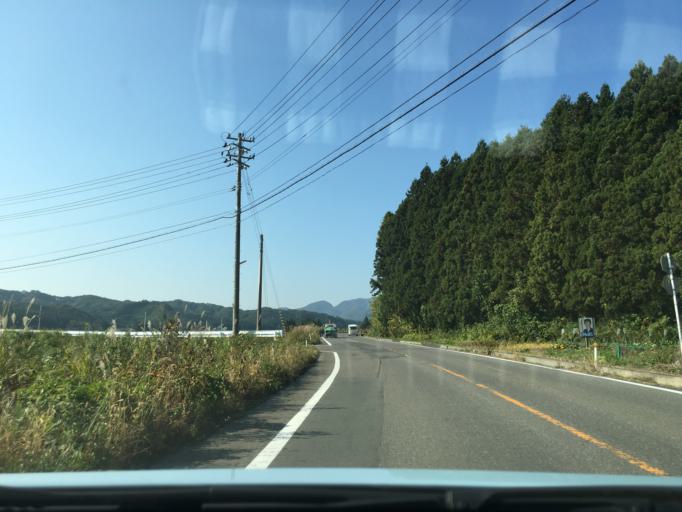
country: JP
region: Fukushima
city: Sukagawa
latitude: 37.2915
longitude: 140.1995
